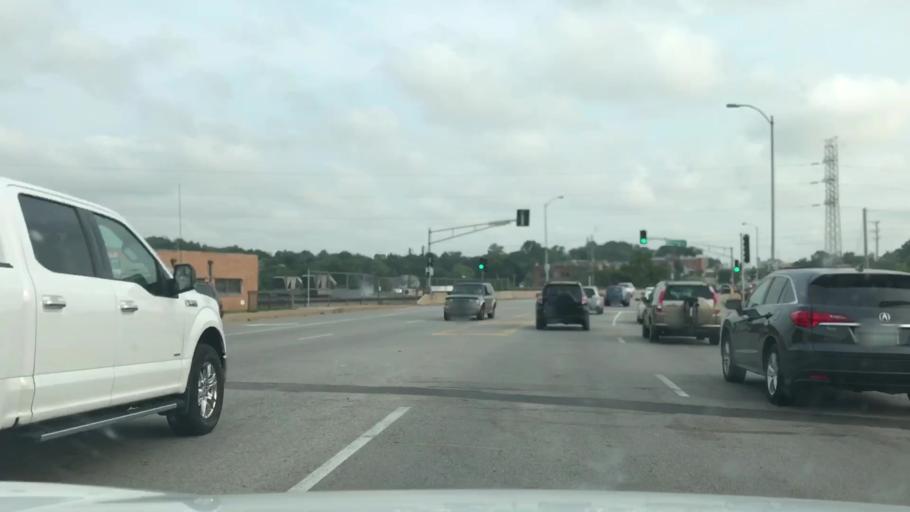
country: US
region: Missouri
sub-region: Saint Louis County
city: Richmond Heights
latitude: 38.6195
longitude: -90.2884
